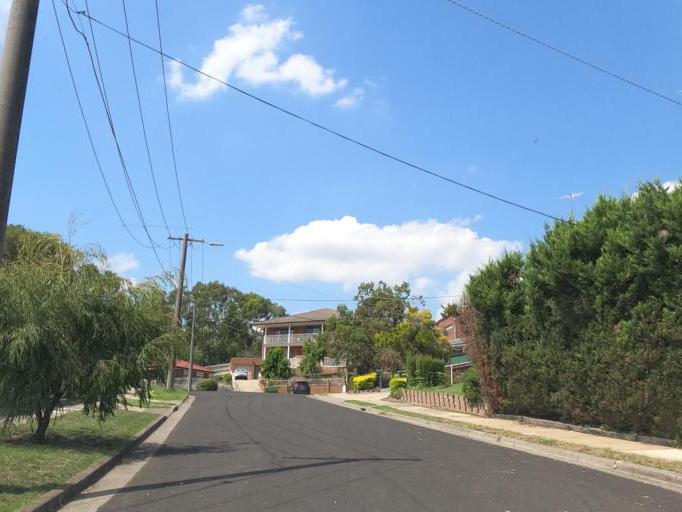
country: AU
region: Victoria
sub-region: Hume
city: Broadmeadows
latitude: -37.6722
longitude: 144.9168
